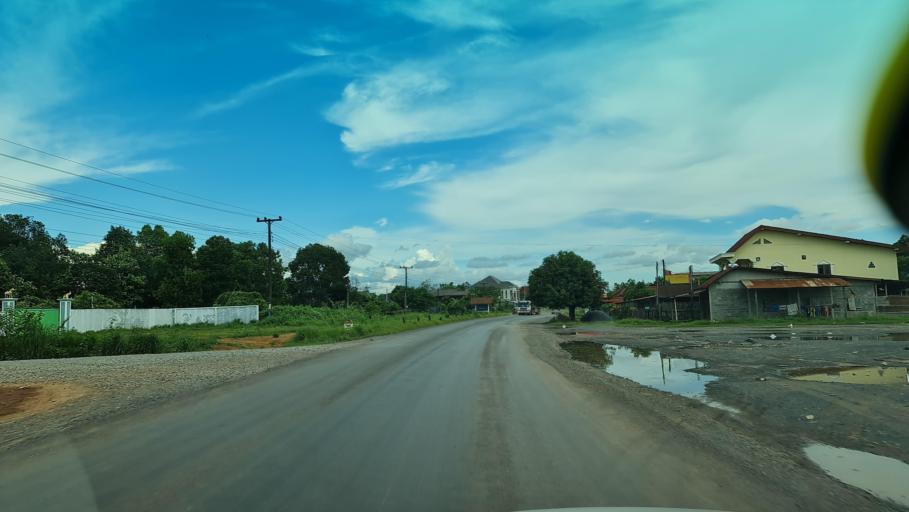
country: LA
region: Bolikhamxai
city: Ban Nahin
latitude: 18.1093
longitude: 104.2787
